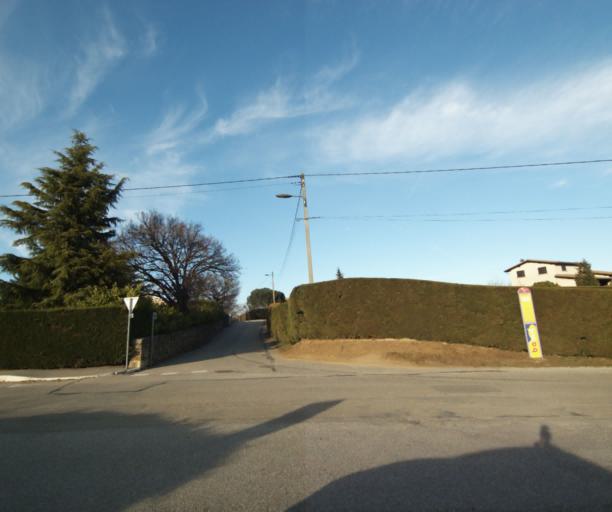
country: FR
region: Rhone-Alpes
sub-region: Departement de l'Ardeche
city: Davezieux
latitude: 45.2584
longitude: 4.7147
